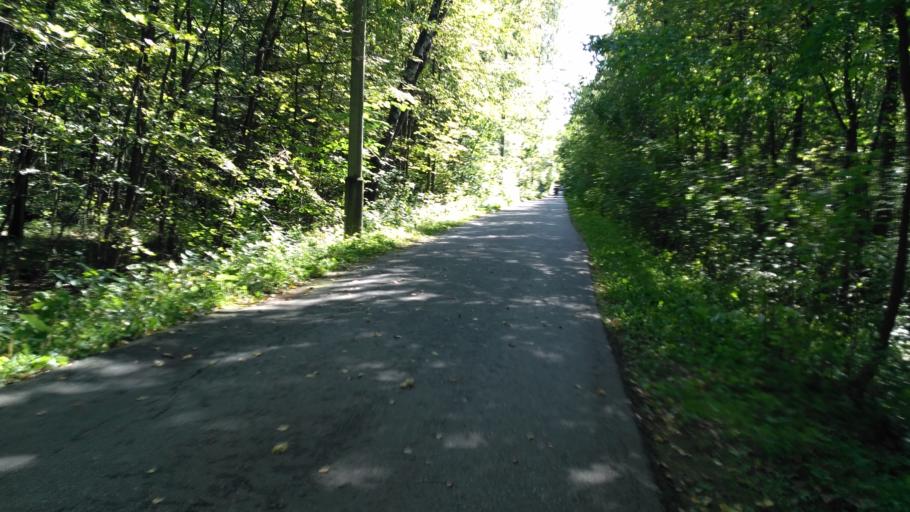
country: RU
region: Moscow
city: Metrogorodok
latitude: 55.7794
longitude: 37.7589
